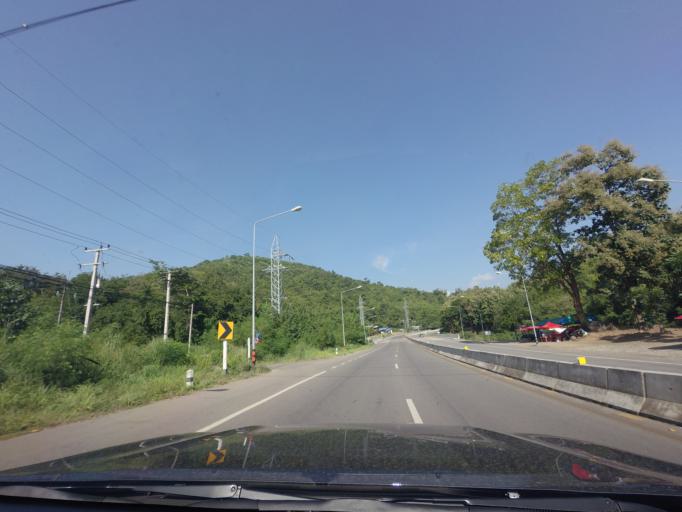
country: TH
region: Phetchabun
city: Lom Sak
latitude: 16.7626
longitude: 101.1424
